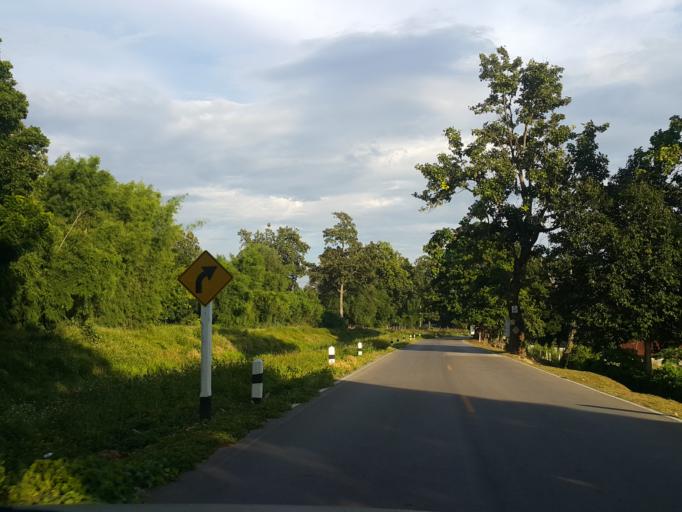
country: TH
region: Chiang Mai
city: San Sai
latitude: 18.8978
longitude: 99.0197
